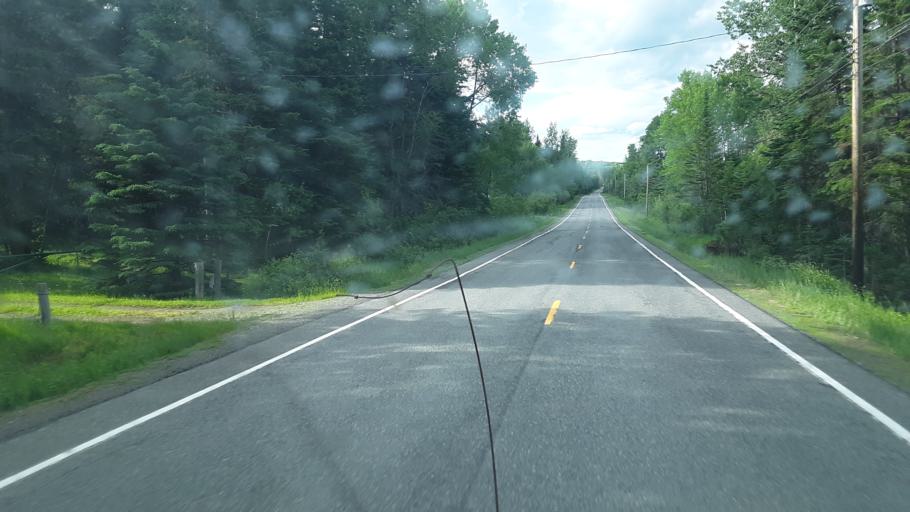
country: US
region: Maine
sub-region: Penobscot County
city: Patten
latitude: 46.1881
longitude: -68.3338
